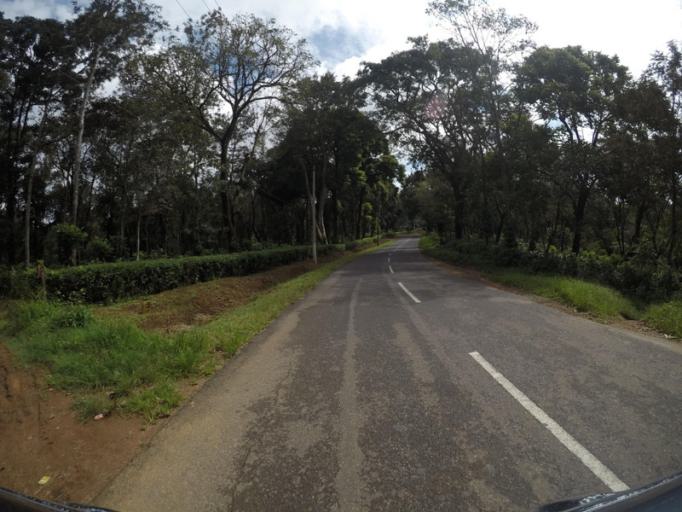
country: IN
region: Karnataka
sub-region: Kodagu
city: Madikeri
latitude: 12.4533
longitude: 75.7608
